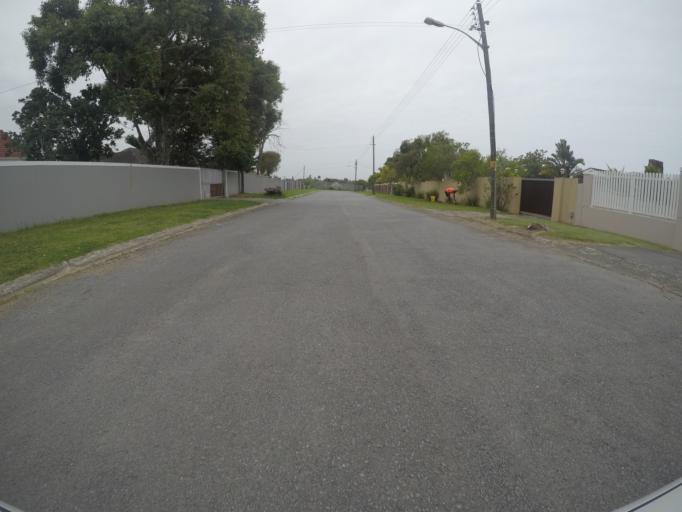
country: ZA
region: Eastern Cape
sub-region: Buffalo City Metropolitan Municipality
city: East London
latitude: -32.9702
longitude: 27.9379
